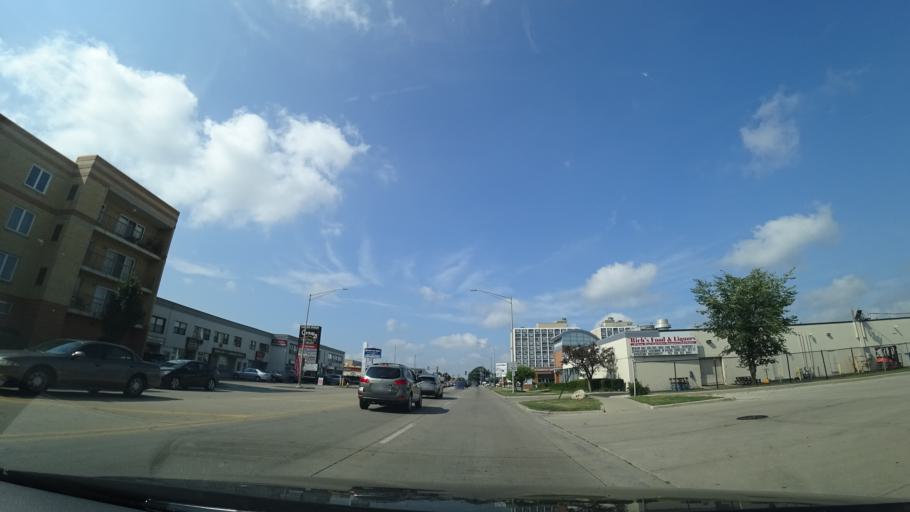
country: US
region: Illinois
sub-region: Cook County
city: Harwood Heights
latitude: 41.9657
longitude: -87.8071
